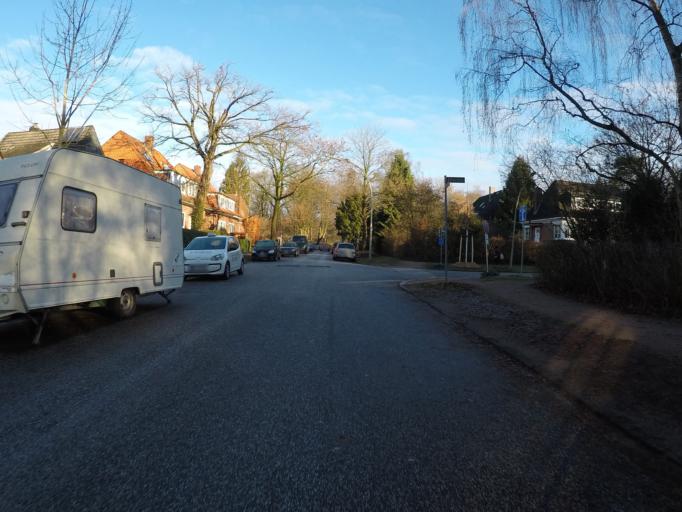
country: DE
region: Hamburg
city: Fuhlsbuettel
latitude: 53.6448
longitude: 10.0240
